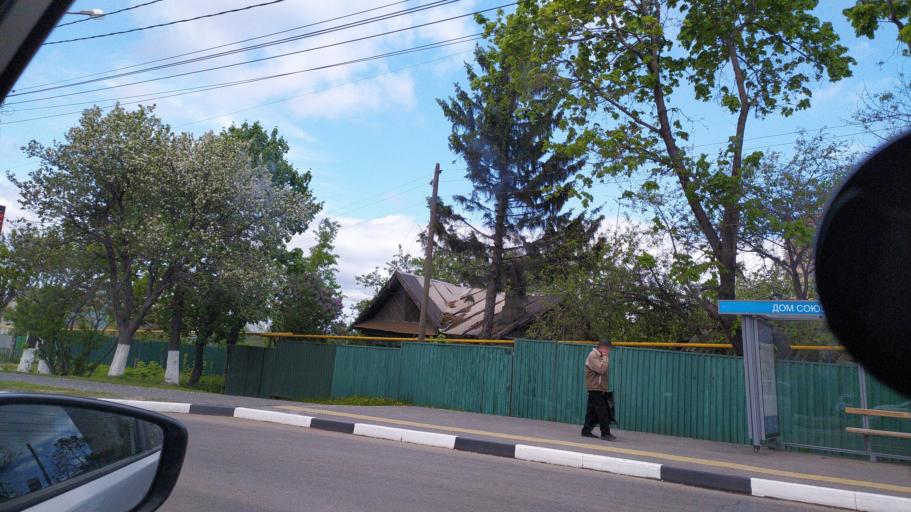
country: RU
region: Chuvashia
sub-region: Cheboksarskiy Rayon
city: Cheboksary
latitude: 56.1409
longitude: 47.2646
